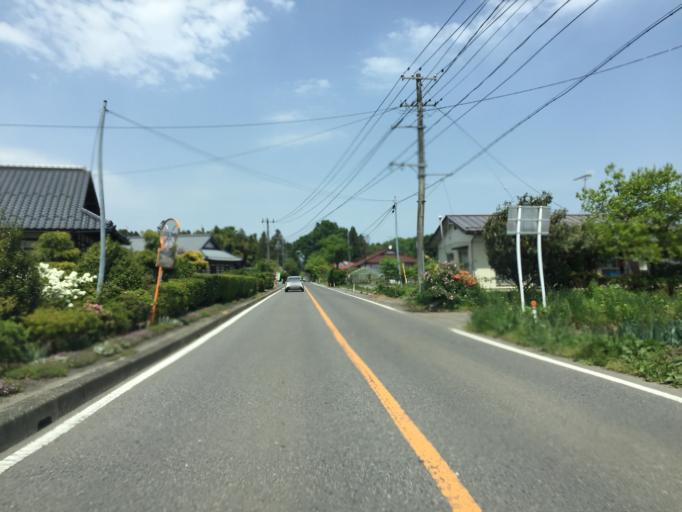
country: JP
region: Fukushima
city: Ishikawa
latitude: 37.1258
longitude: 140.3706
